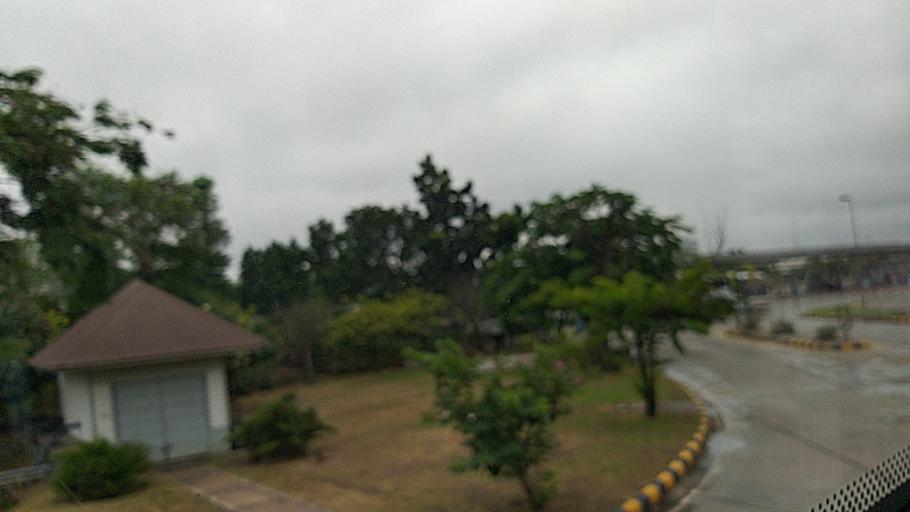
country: TH
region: Nakhon Ratchasima
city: Nakhon Ratchasima
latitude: 14.9932
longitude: 102.0924
